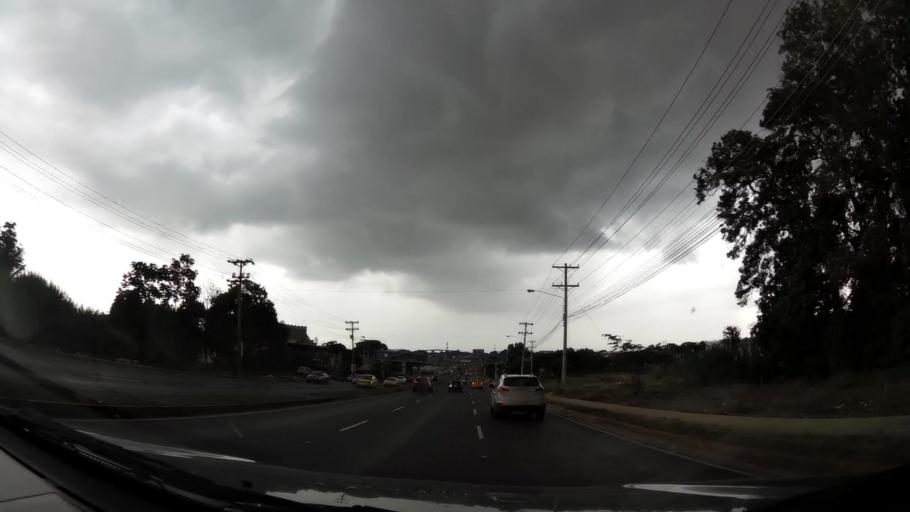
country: PA
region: Panama
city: San Miguelito
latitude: 9.0559
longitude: -79.4371
